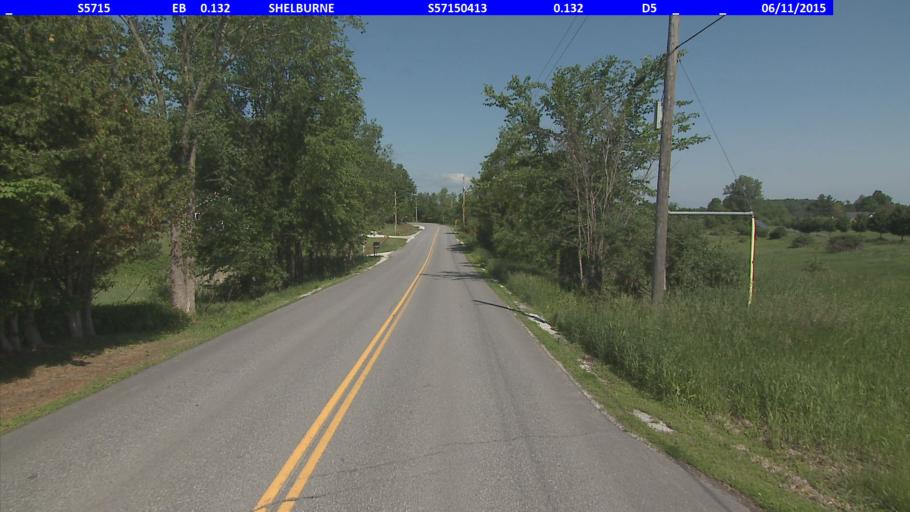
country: US
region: Vermont
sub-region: Chittenden County
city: Hinesburg
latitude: 44.3639
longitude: -73.1637
